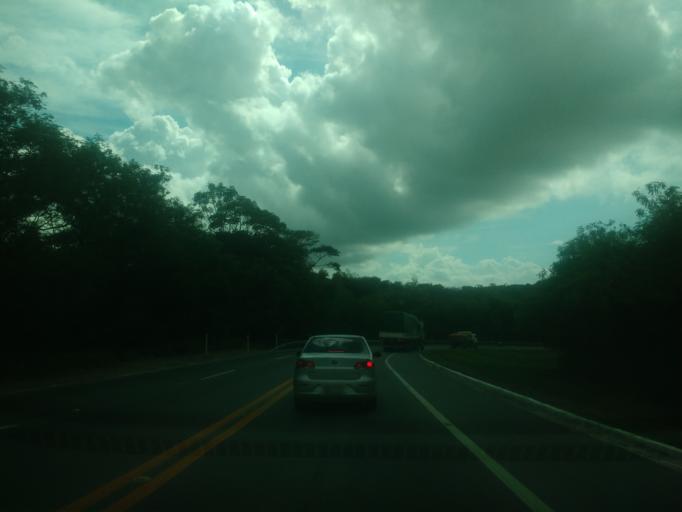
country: BR
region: Alagoas
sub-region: Marechal Deodoro
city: Marechal Deodoro
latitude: -9.6857
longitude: -35.8217
